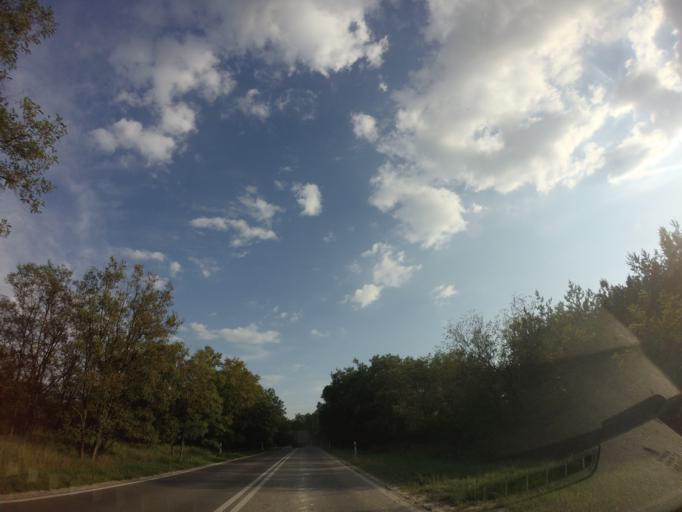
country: PL
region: Lublin Voivodeship
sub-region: Powiat lubartowski
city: Jeziorzany
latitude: 51.5827
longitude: 22.2821
